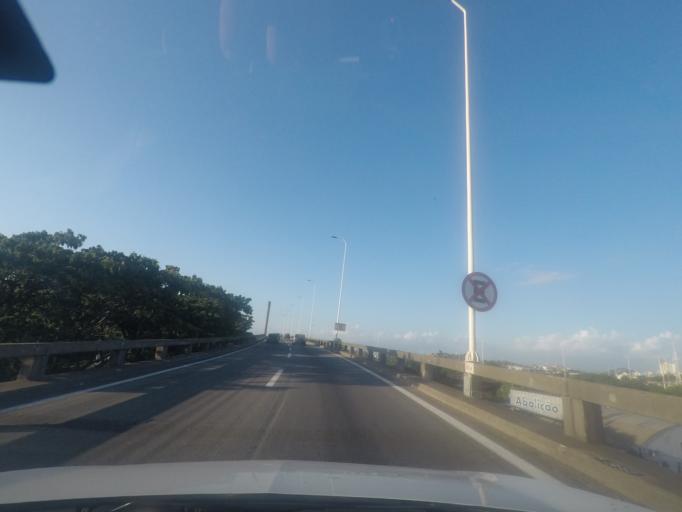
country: BR
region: Rio de Janeiro
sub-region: Niteroi
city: Niteroi
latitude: -22.8826
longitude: -43.1127
